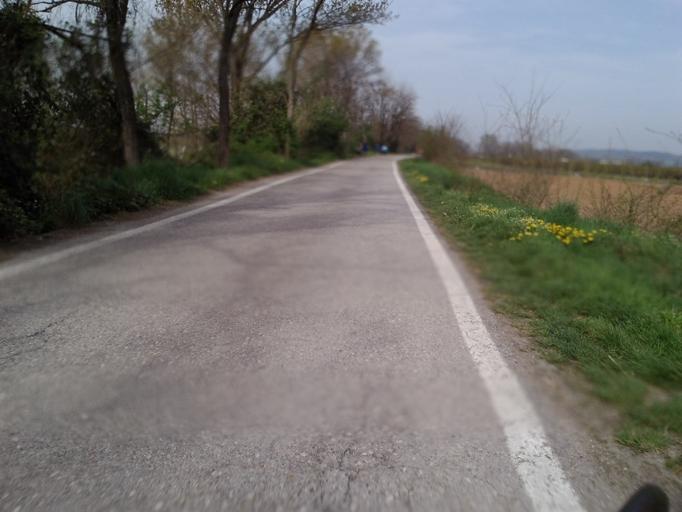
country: IT
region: Veneto
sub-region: Provincia di Verona
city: Rosegaferro
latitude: 45.3555
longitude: 10.8123
